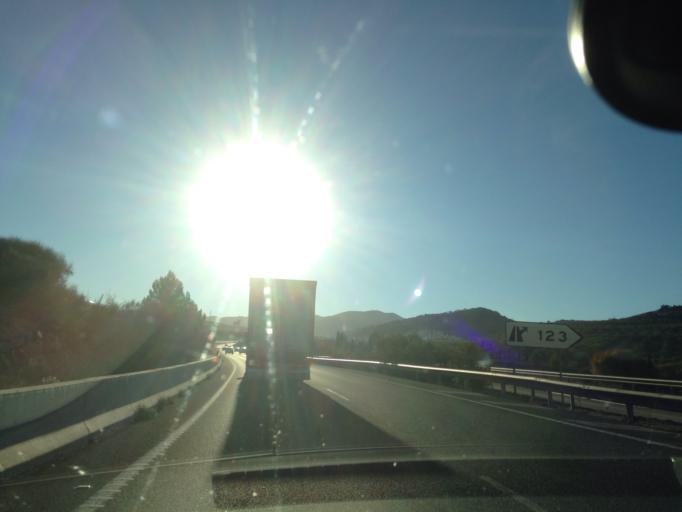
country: ES
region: Andalusia
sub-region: Provincia de Malaga
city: Casabermeja
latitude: 36.9047
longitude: -4.4446
